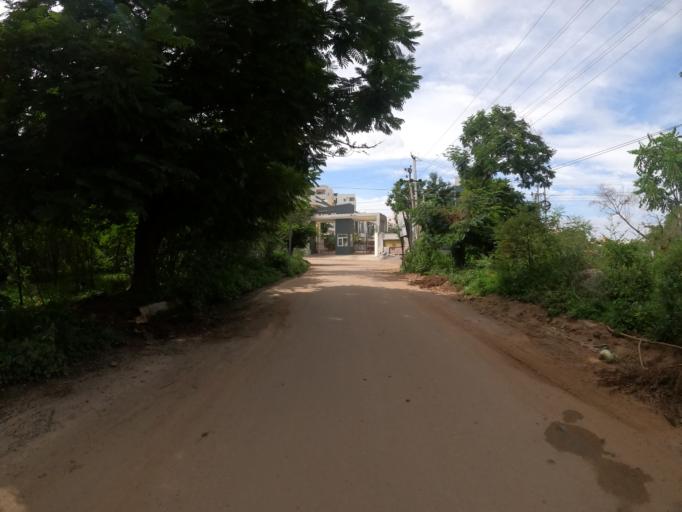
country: IN
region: Telangana
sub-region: Hyderabad
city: Hyderabad
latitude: 17.3538
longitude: 78.3975
